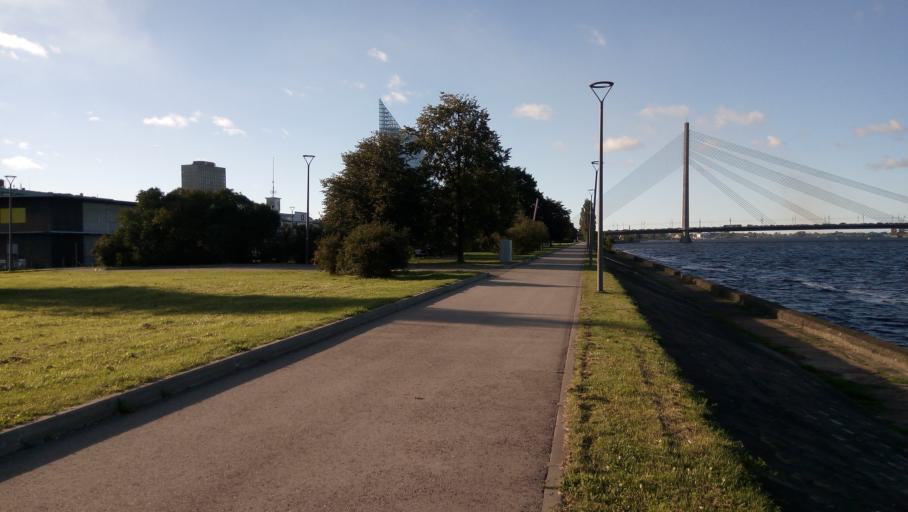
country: LV
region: Riga
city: Riga
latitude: 56.9450
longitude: 24.0963
